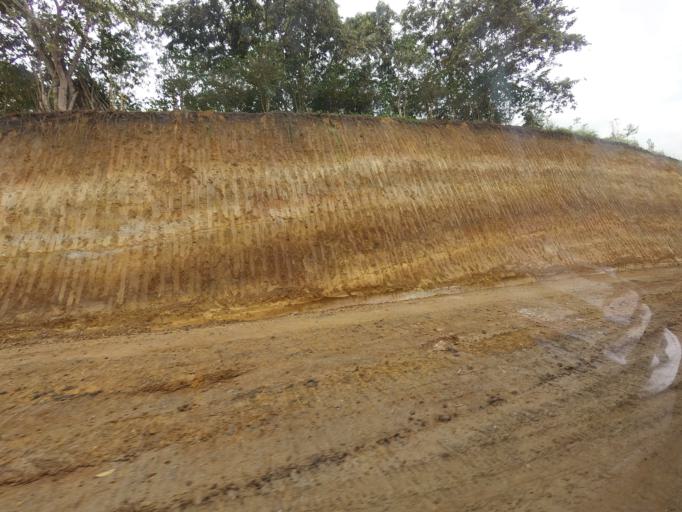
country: CO
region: Huila
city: San Agustin
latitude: 1.9496
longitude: -76.2975
